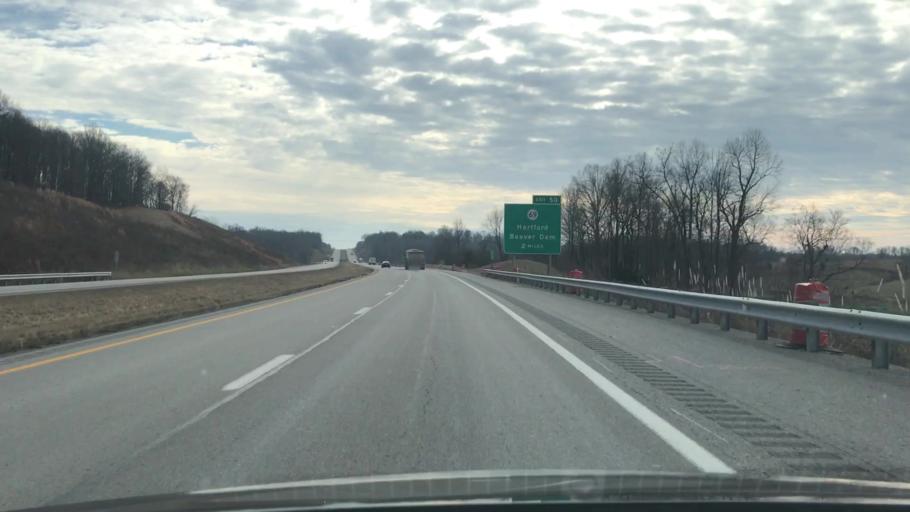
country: US
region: Kentucky
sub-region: Ohio County
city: Hartford
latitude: 37.4822
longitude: -86.9063
